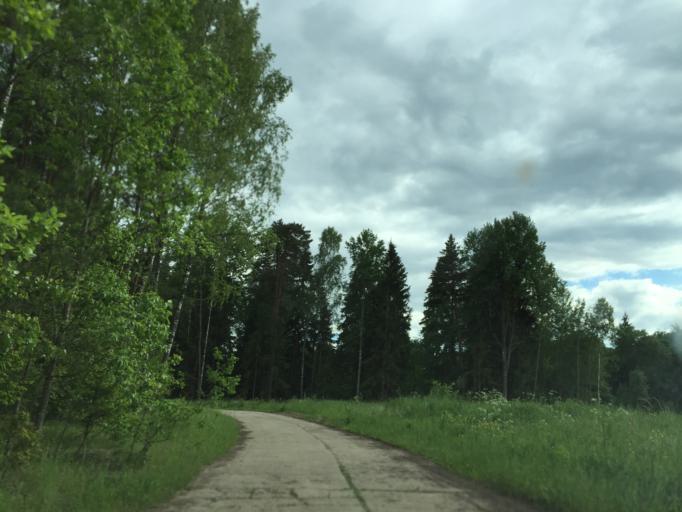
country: LV
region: Dobeles Rajons
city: Dobele
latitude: 56.6407
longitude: 23.1745
